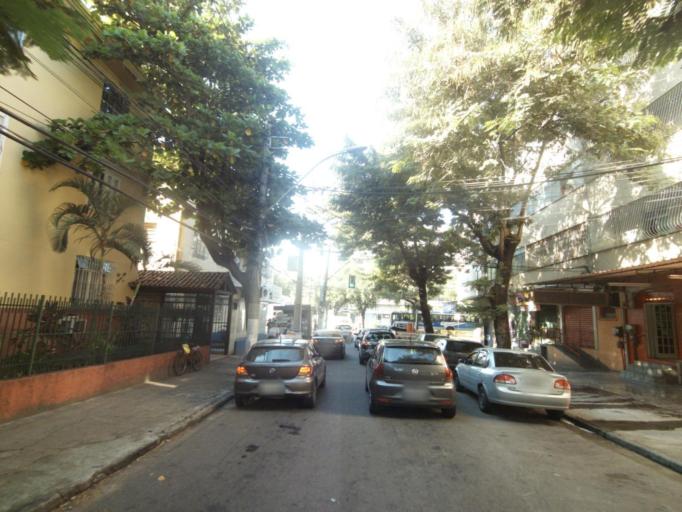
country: BR
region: Rio de Janeiro
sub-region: Niteroi
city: Niteroi
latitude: -22.8805
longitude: -43.0958
